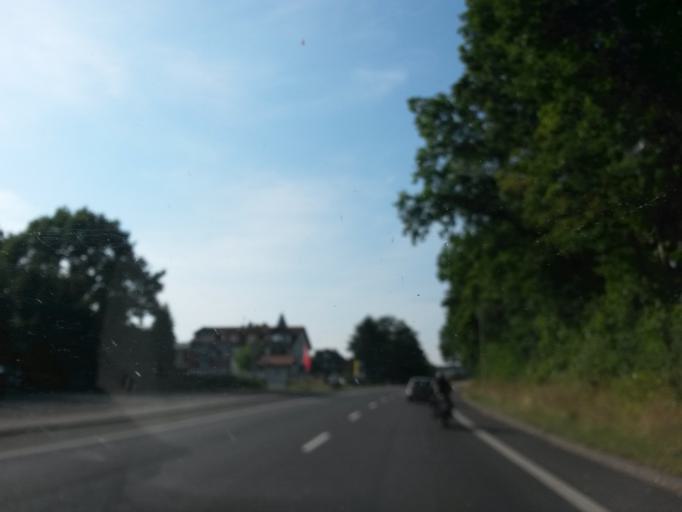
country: DE
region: Hesse
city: Wetter
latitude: 50.9066
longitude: 8.7259
